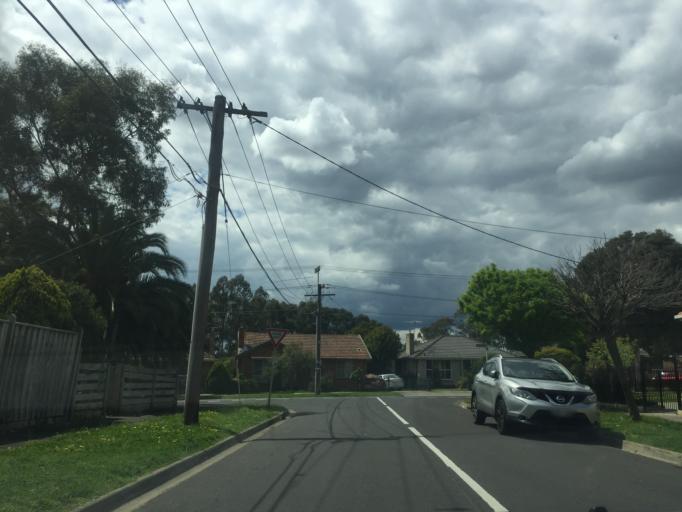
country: AU
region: Victoria
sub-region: Darebin
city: Kingsbury
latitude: -37.7184
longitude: 145.0265
